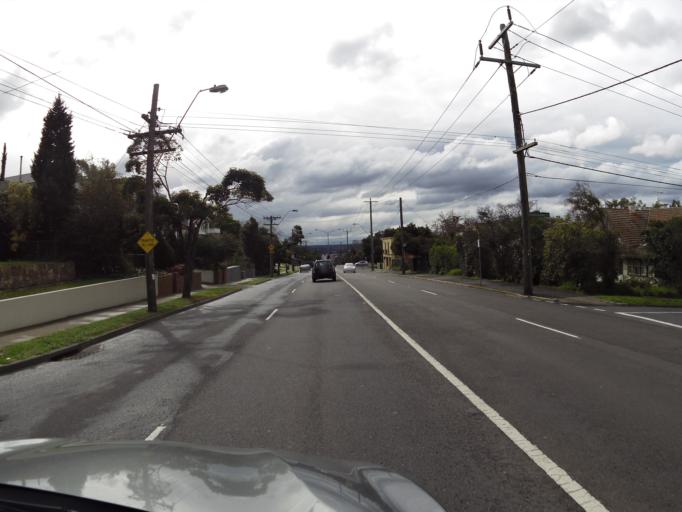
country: AU
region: Victoria
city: Balwyn
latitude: -37.8080
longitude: 145.0611
